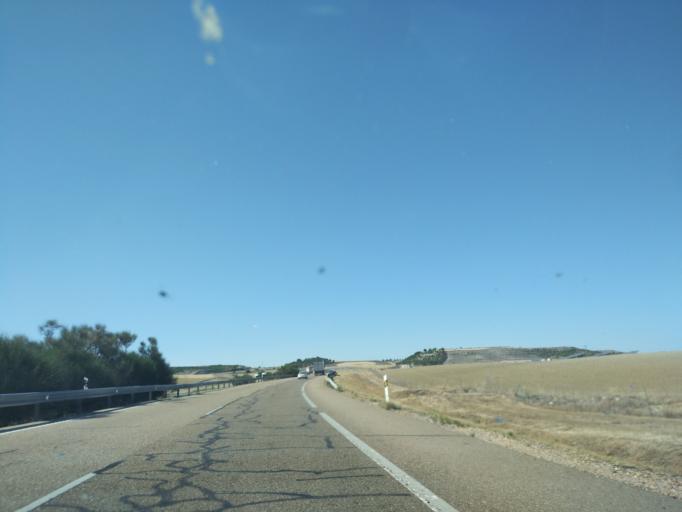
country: ES
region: Castille and Leon
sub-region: Provincia de Valladolid
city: Mota del Marques
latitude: 41.6515
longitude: -5.1914
